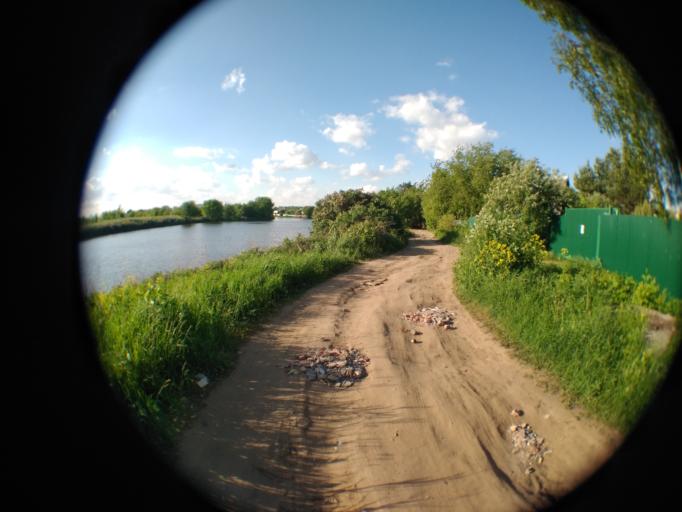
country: RU
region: Moskovskaya
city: Zhukovskiy
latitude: 55.5790
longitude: 38.1025
